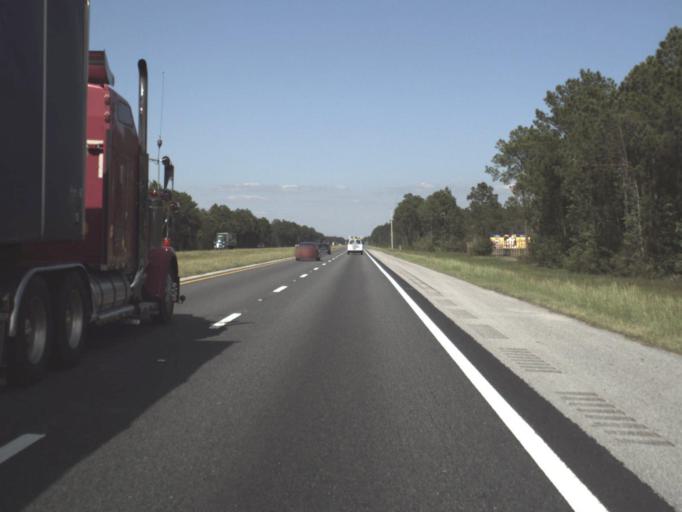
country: US
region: Florida
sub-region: Santa Rosa County
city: Bagdad
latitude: 30.5463
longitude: -87.0618
